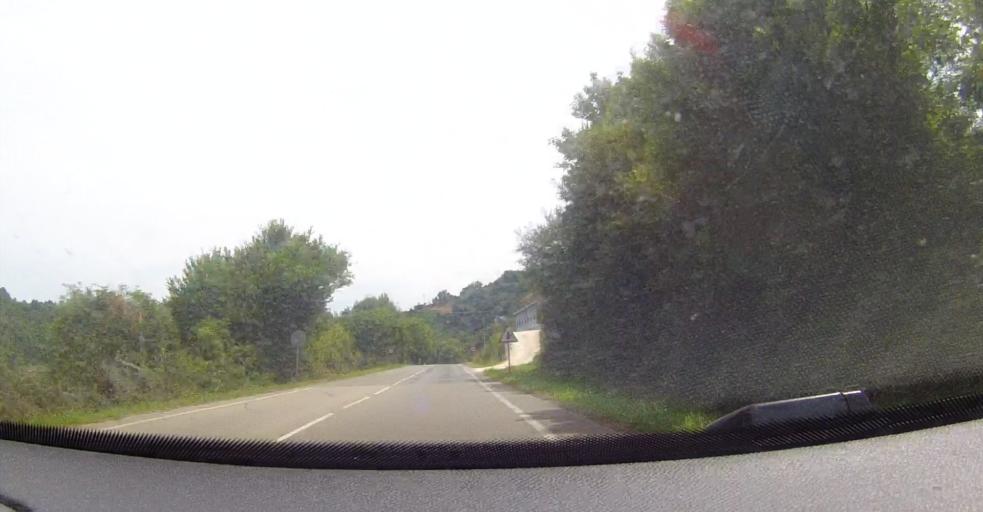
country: ES
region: Asturias
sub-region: Province of Asturias
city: Cangas de Onis
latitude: 43.3505
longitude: -5.1061
